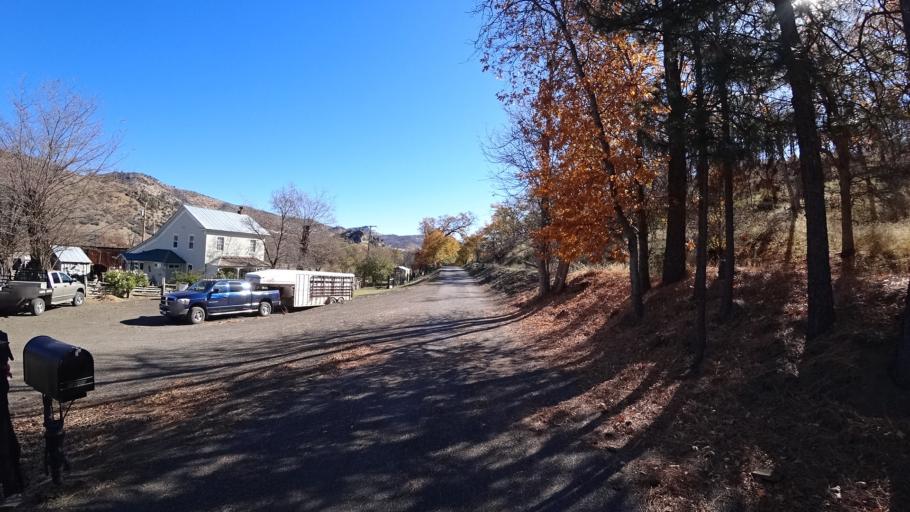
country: US
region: California
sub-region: Siskiyou County
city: Yreka
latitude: 41.9454
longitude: -122.5985
